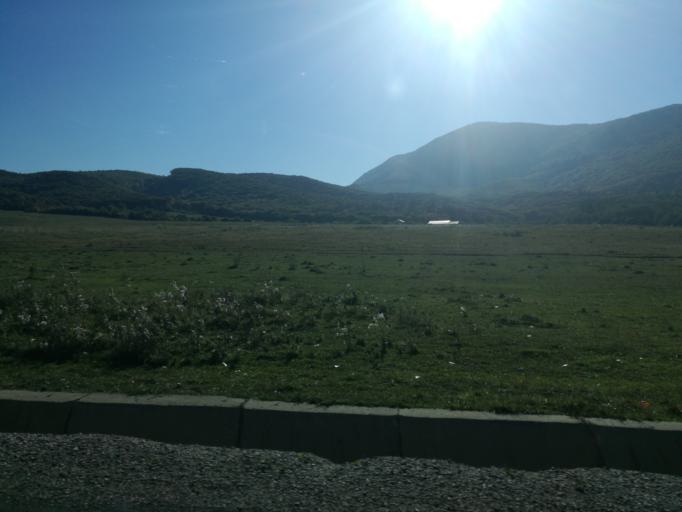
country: RO
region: Brasov
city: Codlea
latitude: 45.7328
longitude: 25.4412
